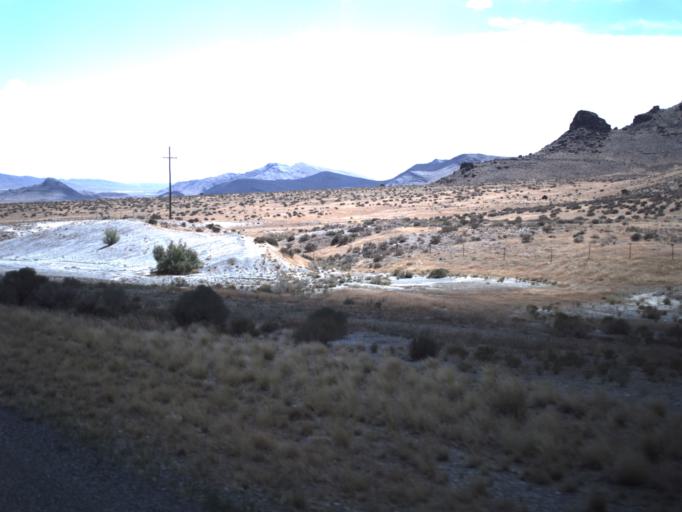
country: US
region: Utah
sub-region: Beaver County
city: Milford
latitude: 39.0854
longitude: -113.5203
